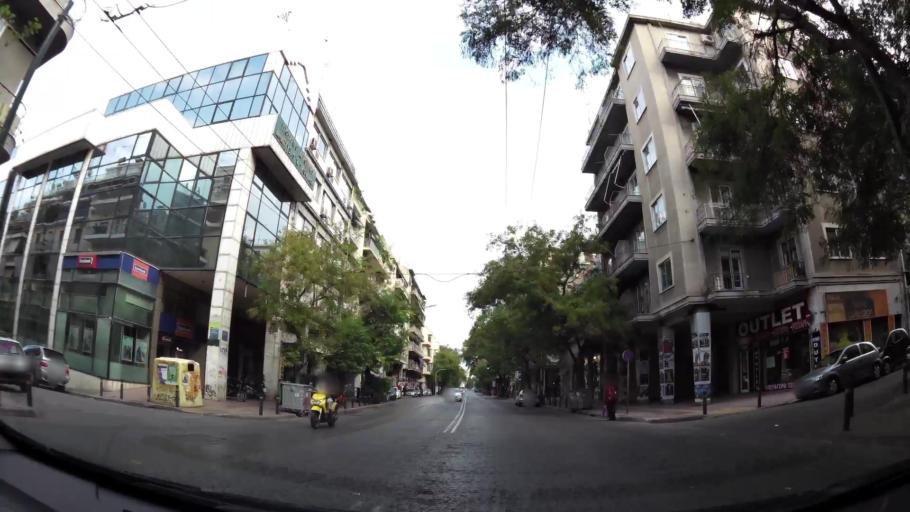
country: GR
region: Attica
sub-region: Nomarchia Athinas
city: Kipseli
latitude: 38.0066
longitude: 23.7351
